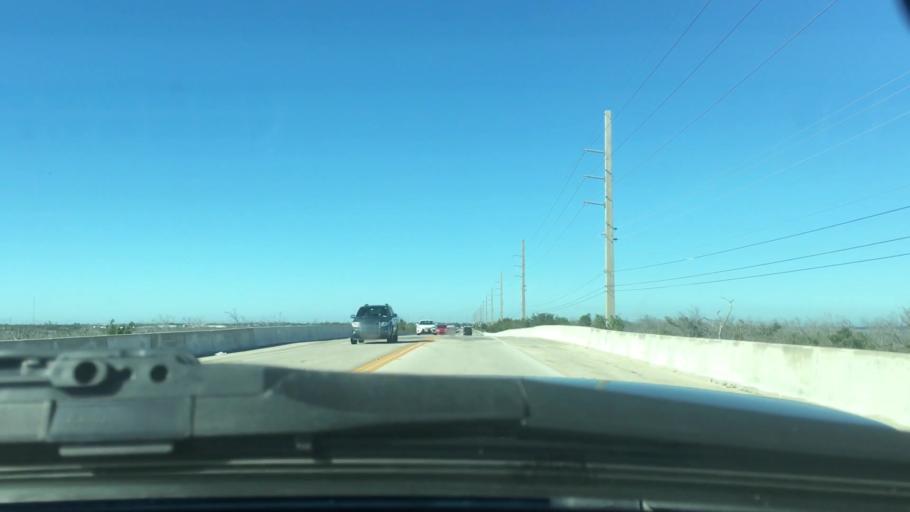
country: US
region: Florida
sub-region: Monroe County
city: Big Pine Key
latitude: 24.6531
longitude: -81.3351
